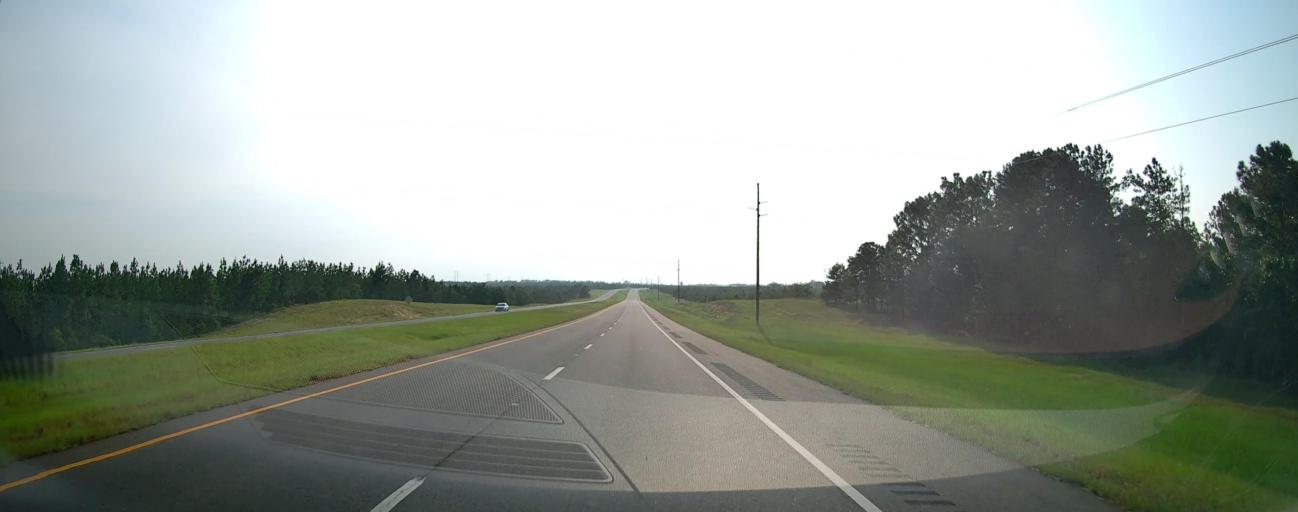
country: US
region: Georgia
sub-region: Talbot County
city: Talbotton
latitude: 32.5948
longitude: -84.4262
